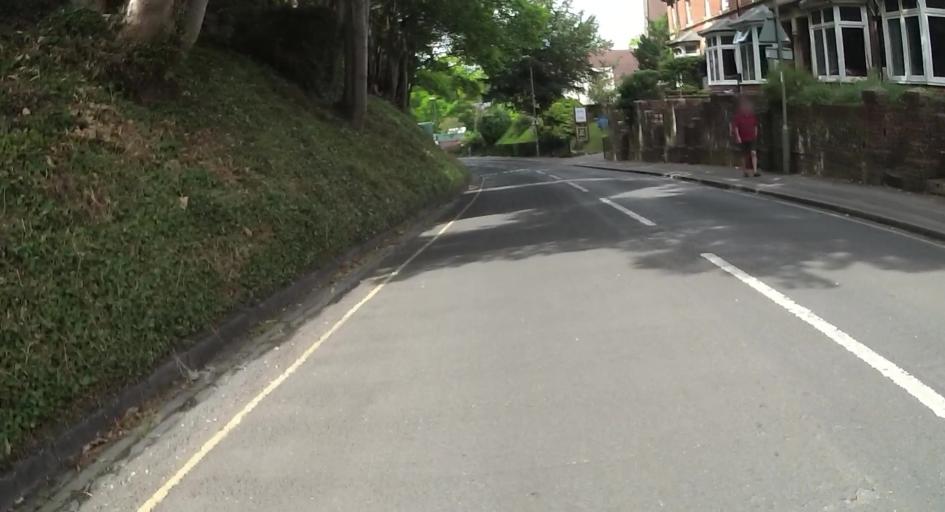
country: GB
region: England
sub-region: Hampshire
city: Winchester
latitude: 51.0660
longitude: -1.3216
